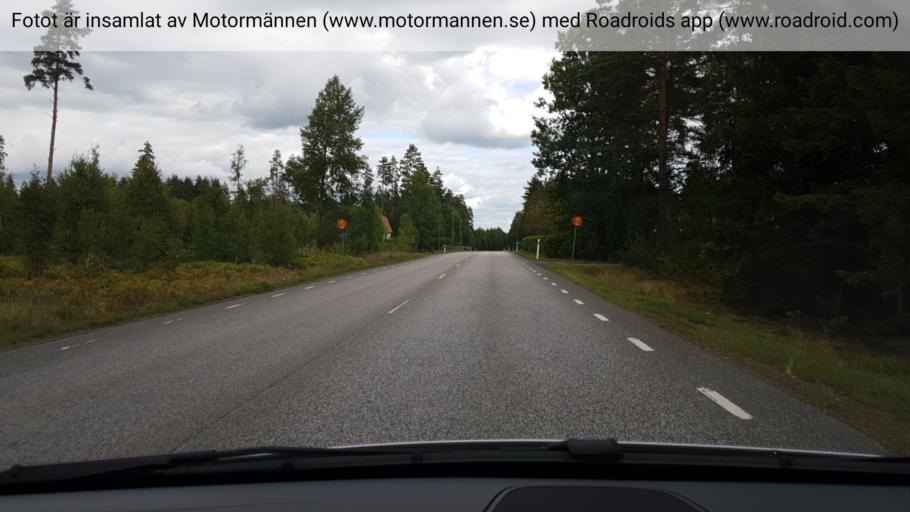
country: SE
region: Vaestra Goetaland
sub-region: Tidaholms Kommun
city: Tidaholm
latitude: 58.1451
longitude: 13.9103
